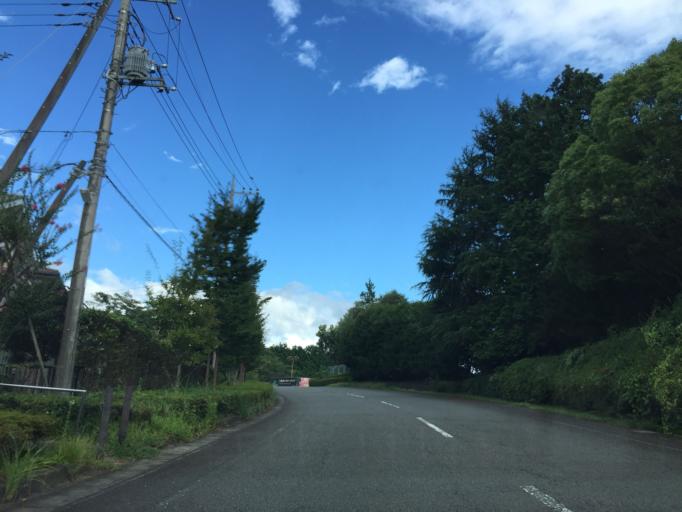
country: JP
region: Shizuoka
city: Mishima
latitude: 35.1615
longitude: 138.9475
